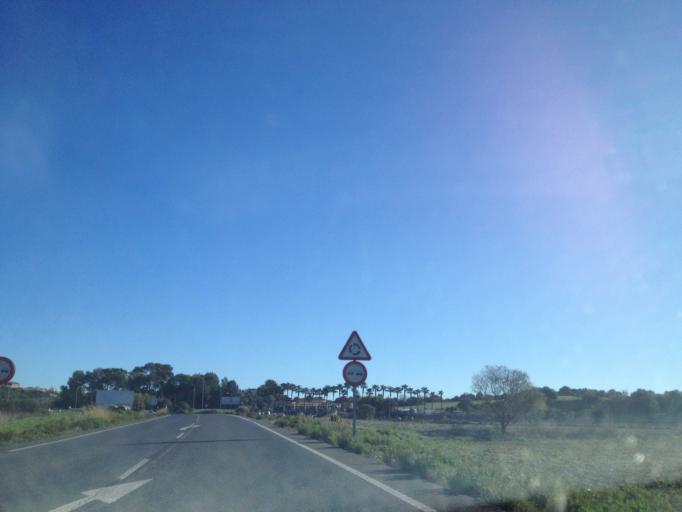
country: ES
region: Balearic Islands
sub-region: Illes Balears
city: Ariany
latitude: 39.6458
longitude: 3.0969
